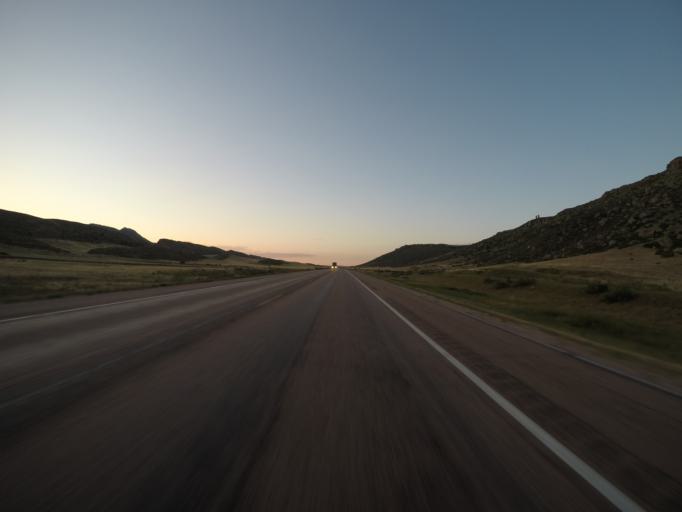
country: US
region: Colorado
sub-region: Larimer County
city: Laporte
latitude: 40.7049
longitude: -105.1735
